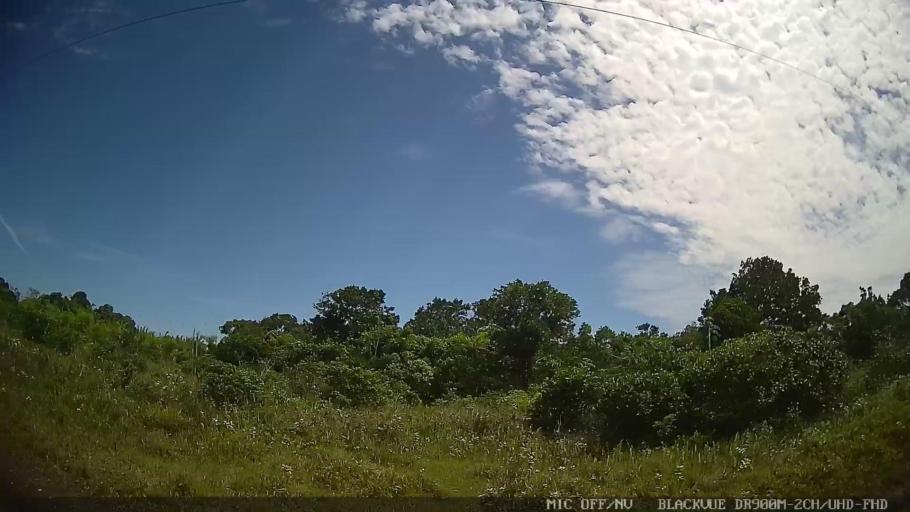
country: BR
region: Sao Paulo
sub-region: Iguape
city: Iguape
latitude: -24.7143
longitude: -47.5079
